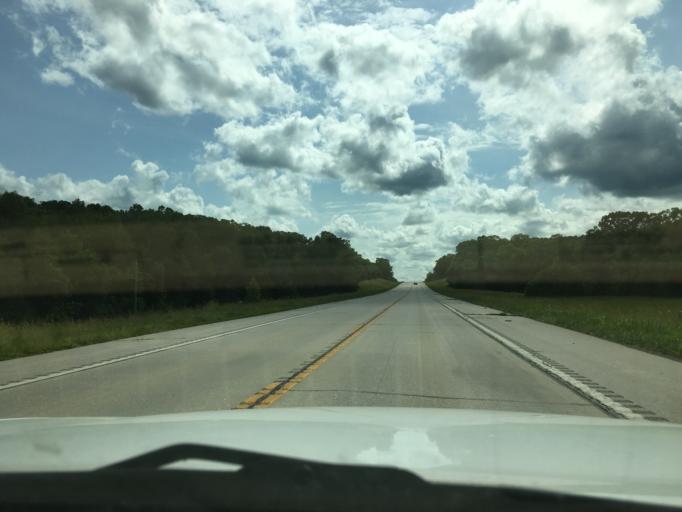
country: US
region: Missouri
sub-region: Franklin County
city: Gerald
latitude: 38.4206
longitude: -91.2868
